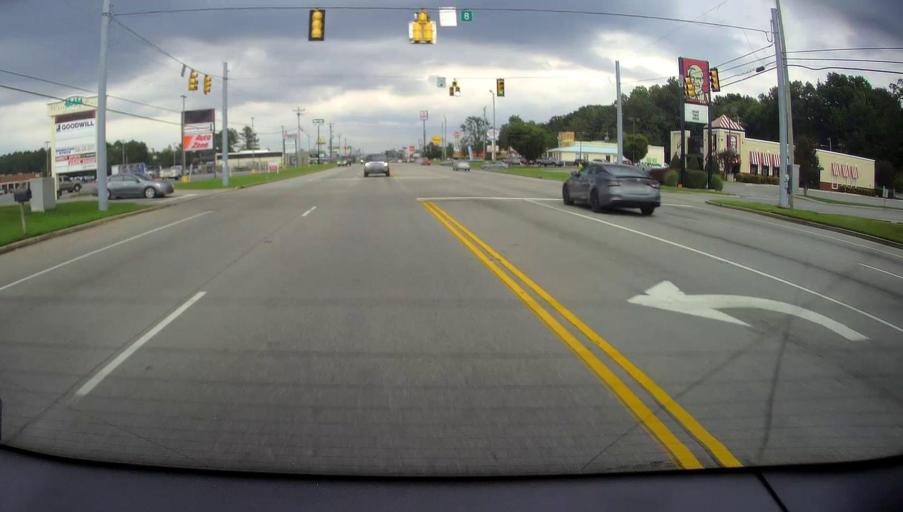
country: US
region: Tennessee
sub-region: Coffee County
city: Manchester
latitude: 35.4605
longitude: -86.0599
